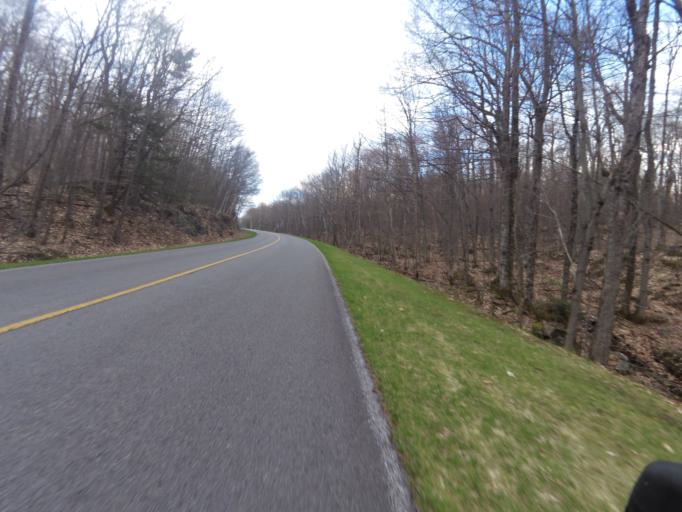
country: CA
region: Quebec
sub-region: Outaouais
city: Gatineau
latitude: 45.4760
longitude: -75.8455
